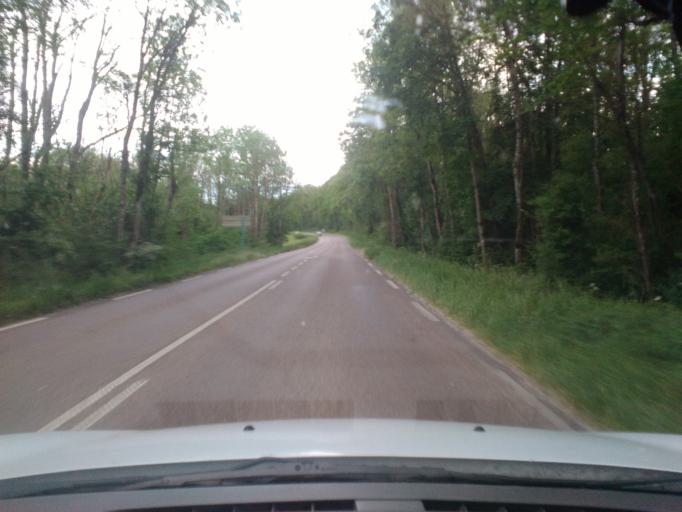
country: FR
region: Lorraine
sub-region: Departement des Vosges
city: Mirecourt
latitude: 48.3060
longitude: 6.0708
